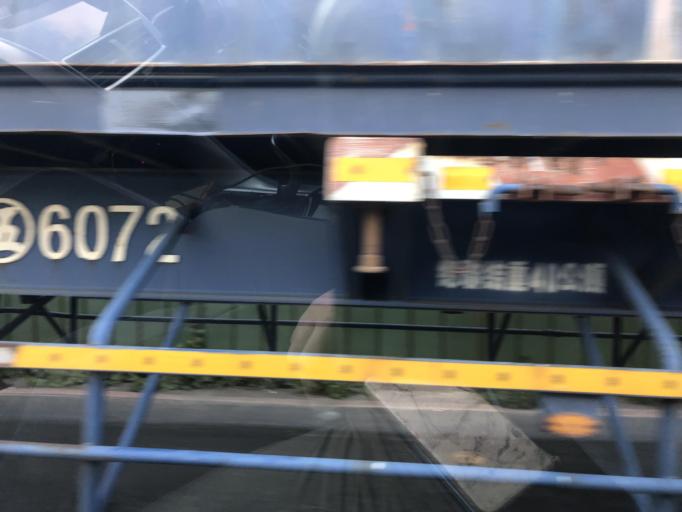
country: TW
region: Taiwan
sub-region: Tainan
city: Tainan
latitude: 23.0438
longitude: 120.2463
